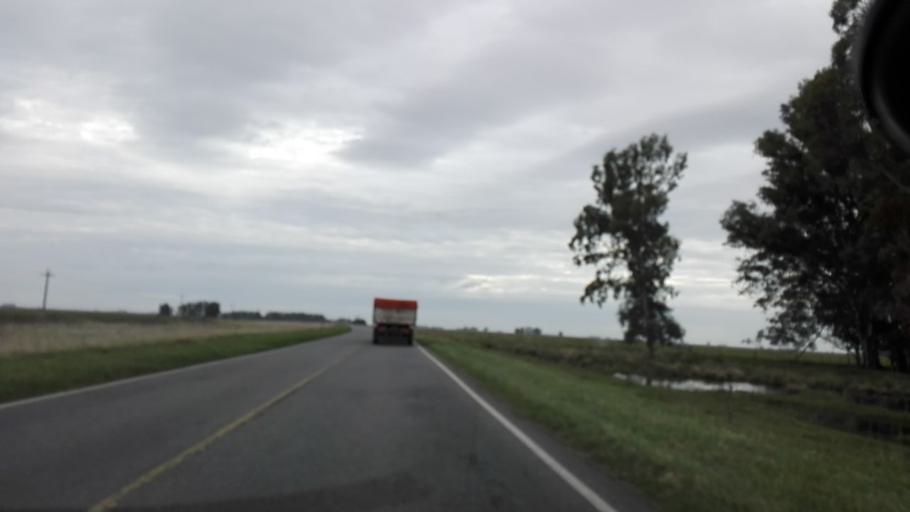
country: AR
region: Buenos Aires
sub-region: Partido de Rauch
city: Rauch
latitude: -36.5461
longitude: -59.0446
